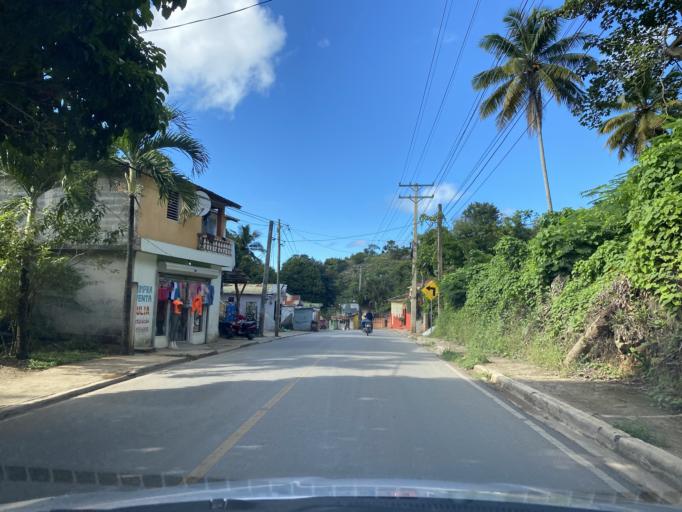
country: DO
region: Samana
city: Las Terrenas
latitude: 19.2961
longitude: -69.5503
